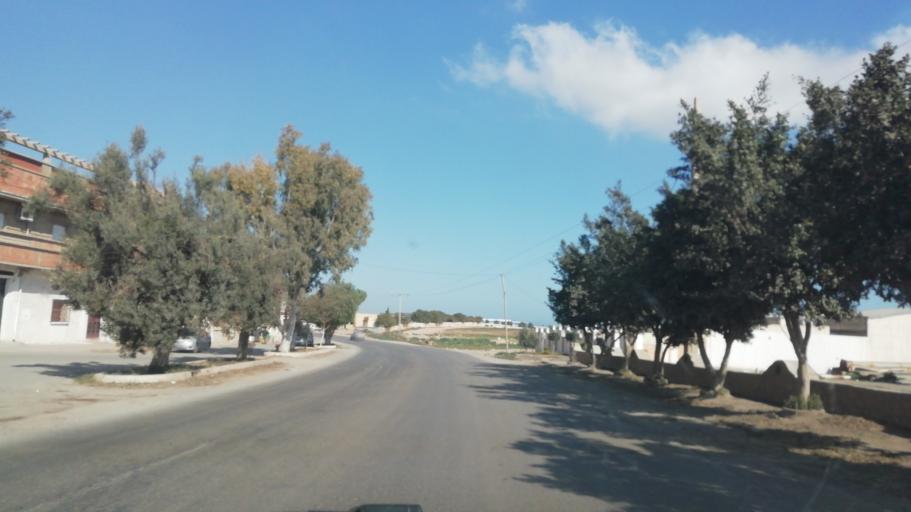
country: DZ
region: Oran
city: Ain el Bya
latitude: 35.7772
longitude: -0.2791
